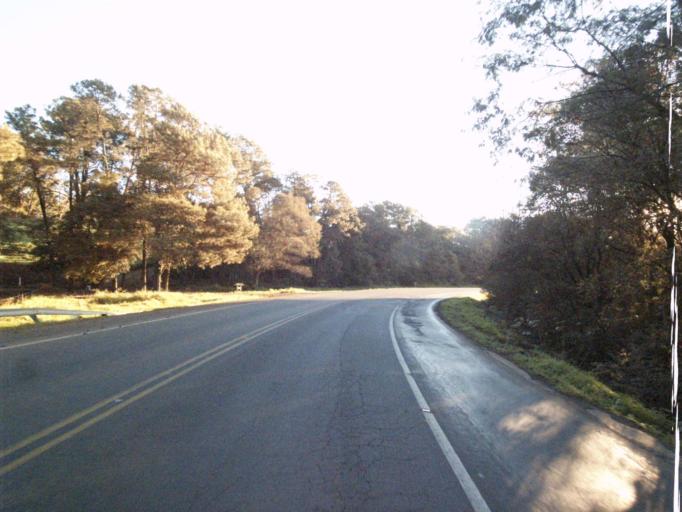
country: BR
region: Santa Catarina
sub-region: Chapeco
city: Chapeco
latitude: -26.8322
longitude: -53.0216
